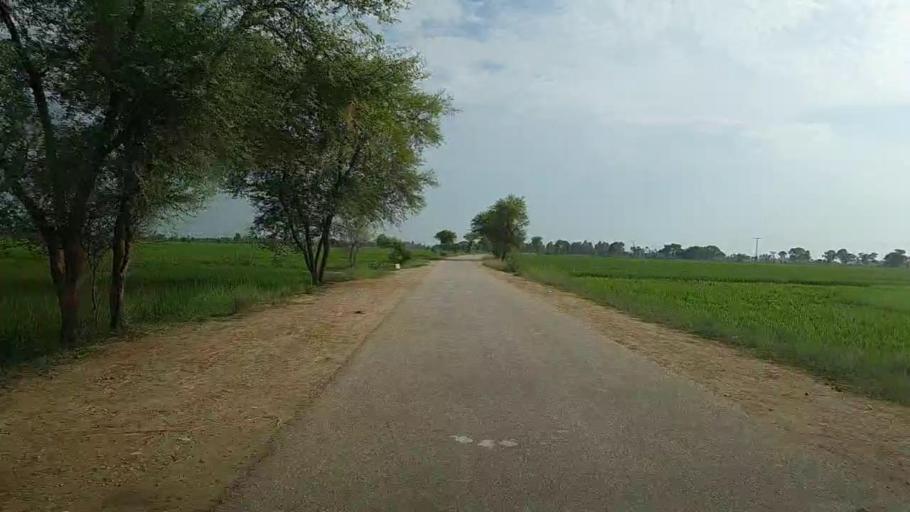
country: PK
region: Sindh
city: Thul
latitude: 28.2622
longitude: 68.8593
